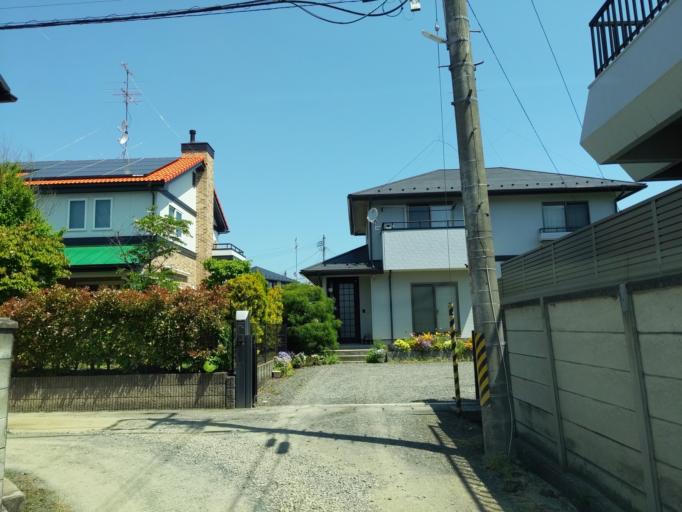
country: JP
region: Fukushima
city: Koriyama
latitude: 37.3899
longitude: 140.3449
